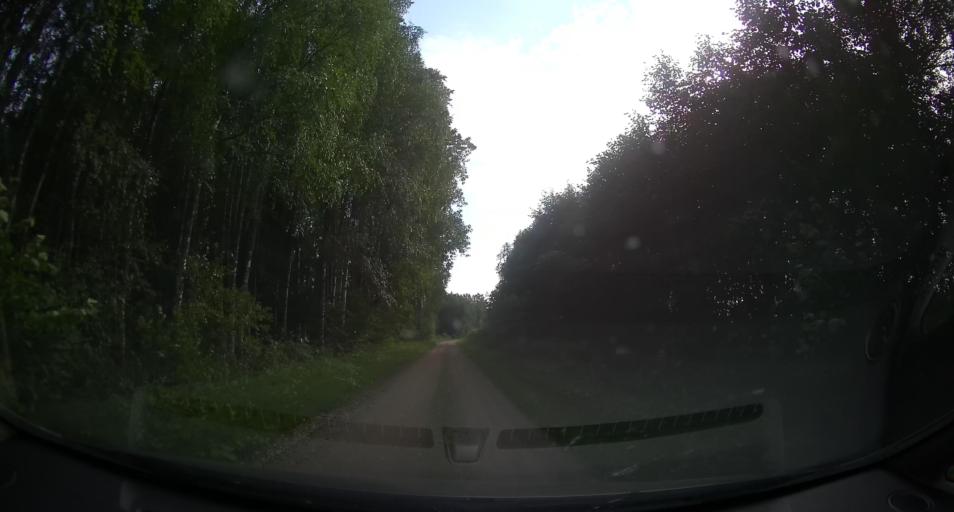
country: EE
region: Laeaene
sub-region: Lihula vald
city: Lihula
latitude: 58.6522
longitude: 23.7954
